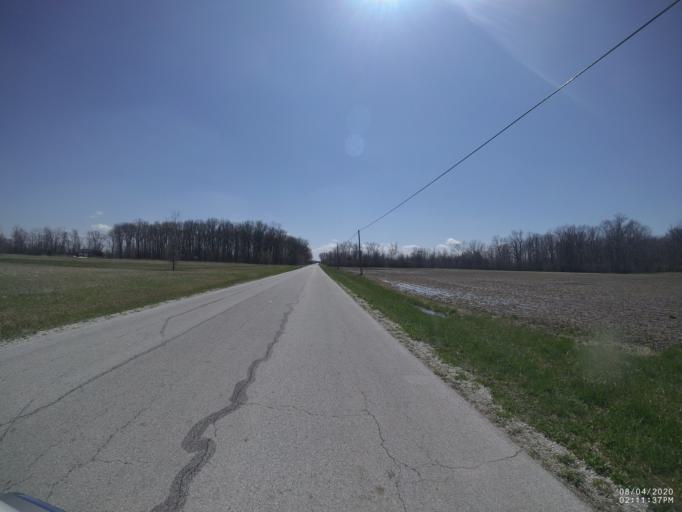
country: US
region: Ohio
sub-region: Sandusky County
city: Gibsonburg
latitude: 41.2622
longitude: -83.2644
